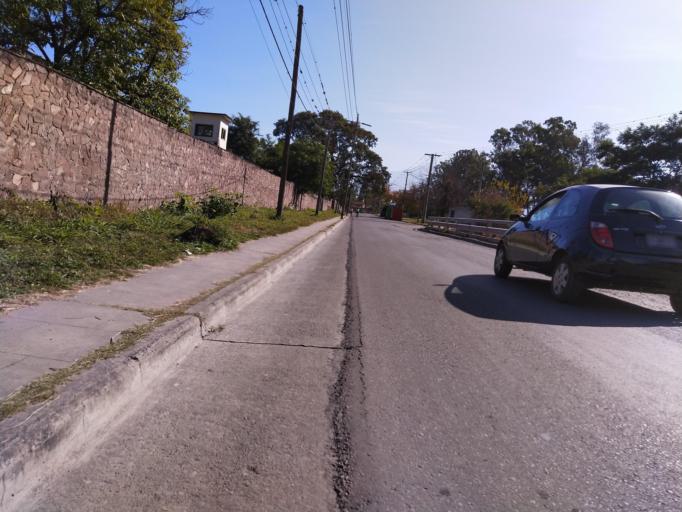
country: AR
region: Jujuy
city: San Salvador de Jujuy
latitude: -24.1794
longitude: -65.3212
